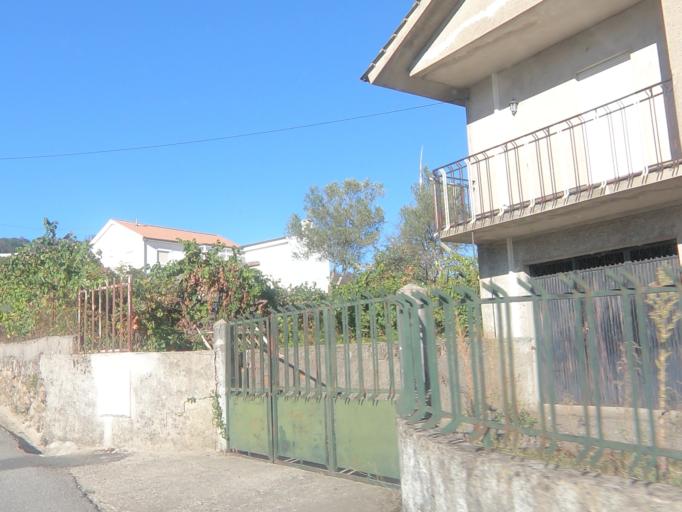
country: PT
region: Vila Real
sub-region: Vila Real
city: Vila Real
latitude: 41.3197
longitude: -7.7679
